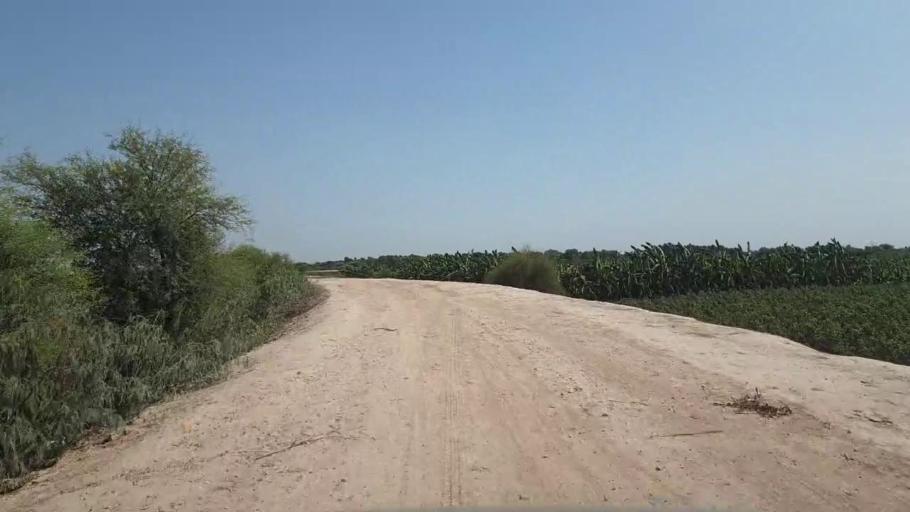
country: PK
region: Sindh
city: Matiari
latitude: 25.6295
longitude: 68.4741
